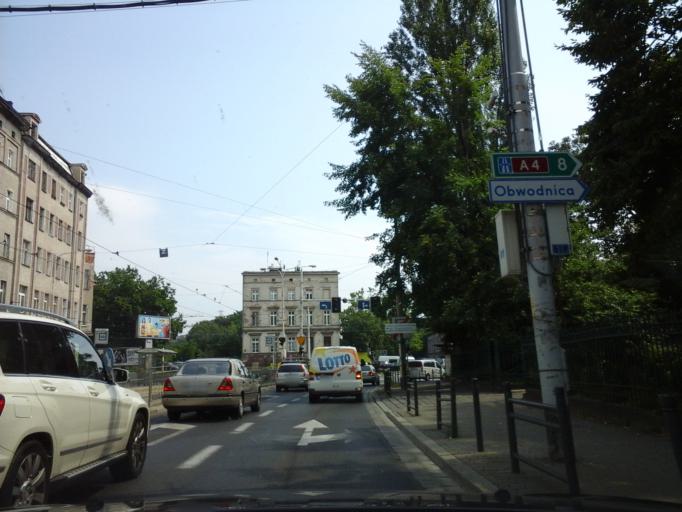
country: PL
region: Lower Silesian Voivodeship
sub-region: Powiat wroclawski
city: Wroclaw
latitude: 51.0984
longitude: 17.0424
